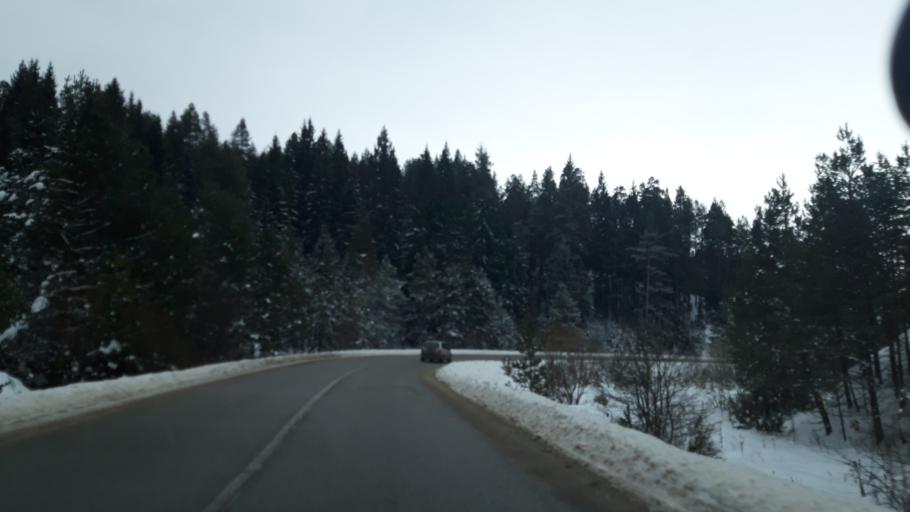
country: BA
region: Republika Srpska
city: Sokolac
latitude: 43.9832
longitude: 18.8620
